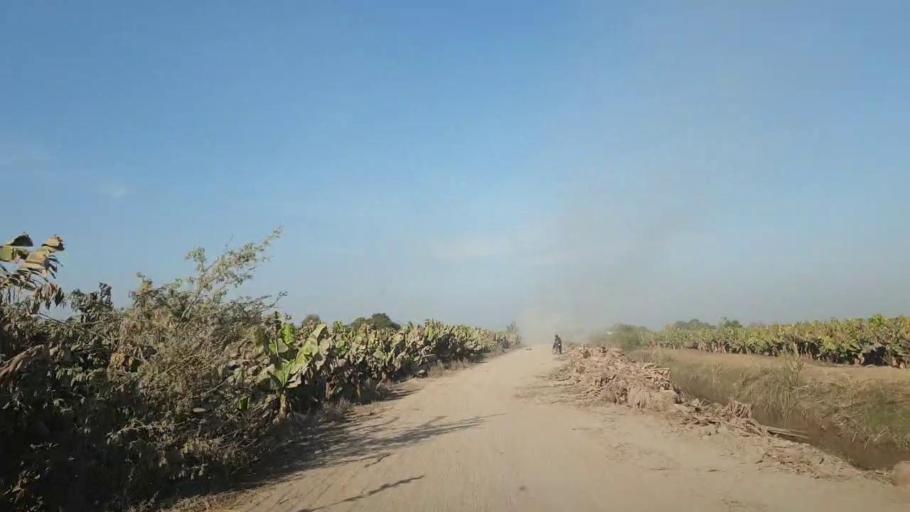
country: PK
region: Sindh
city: Tando Adam
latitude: 25.7068
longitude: 68.7023
